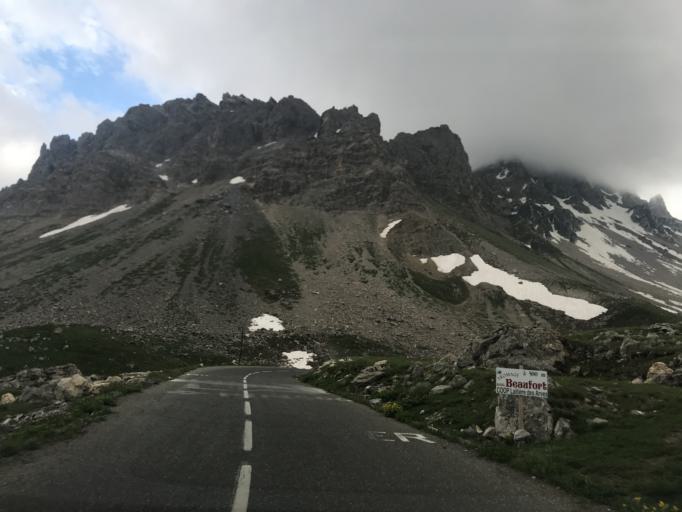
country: FR
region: Rhone-Alpes
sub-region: Departement de la Savoie
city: Valloire
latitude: 45.0806
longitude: 6.4262
